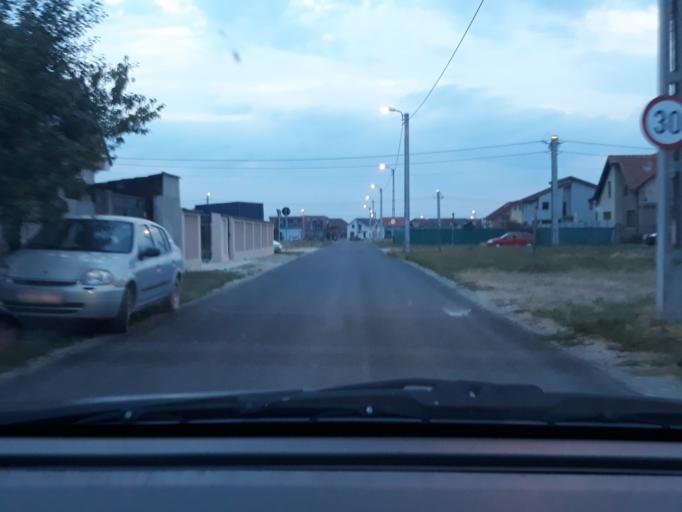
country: RO
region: Bihor
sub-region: Comuna Biharea
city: Oradea
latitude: 47.0260
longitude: 21.9273
